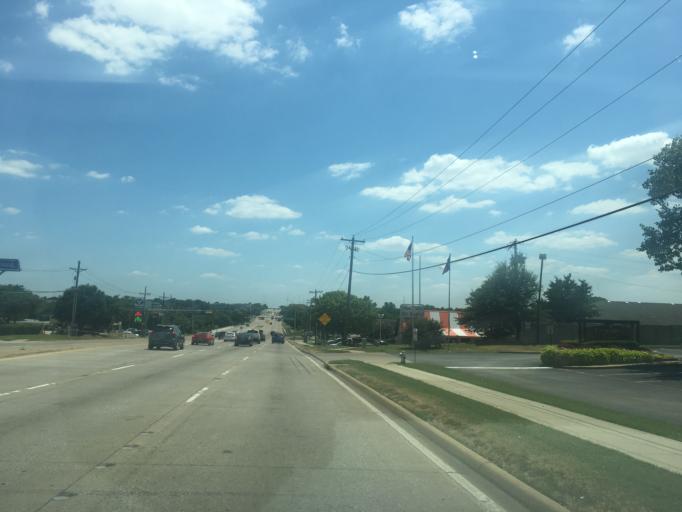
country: US
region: Texas
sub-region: Denton County
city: Lewisville
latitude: 33.0205
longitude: -96.9931
